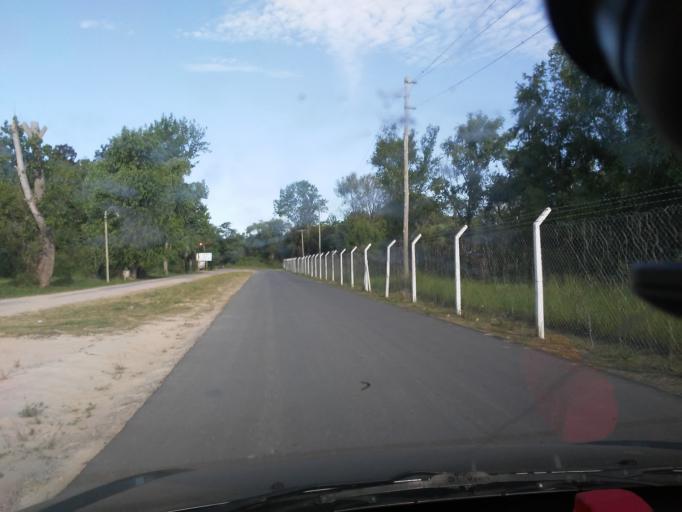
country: AR
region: Buenos Aires
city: Belen de Escobar
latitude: -34.2493
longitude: -58.7297
